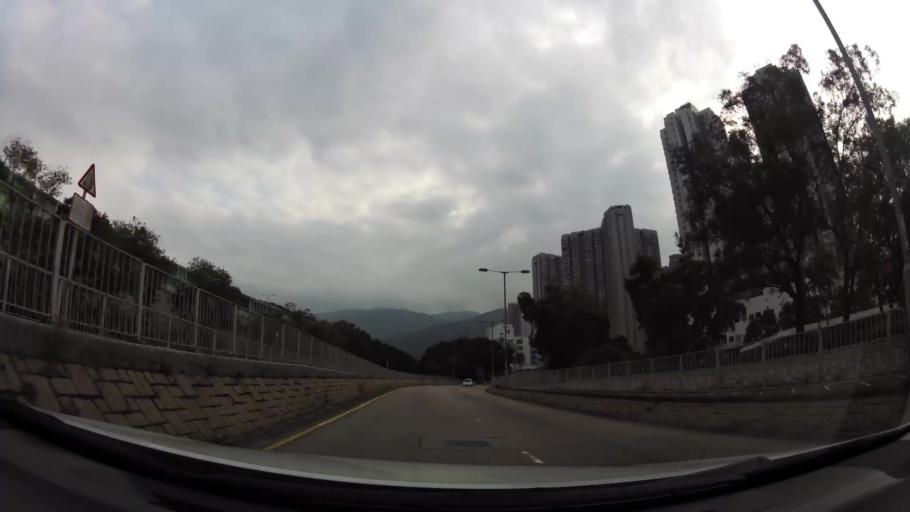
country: HK
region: Tai Po
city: Tai Po
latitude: 22.4434
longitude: 114.1711
